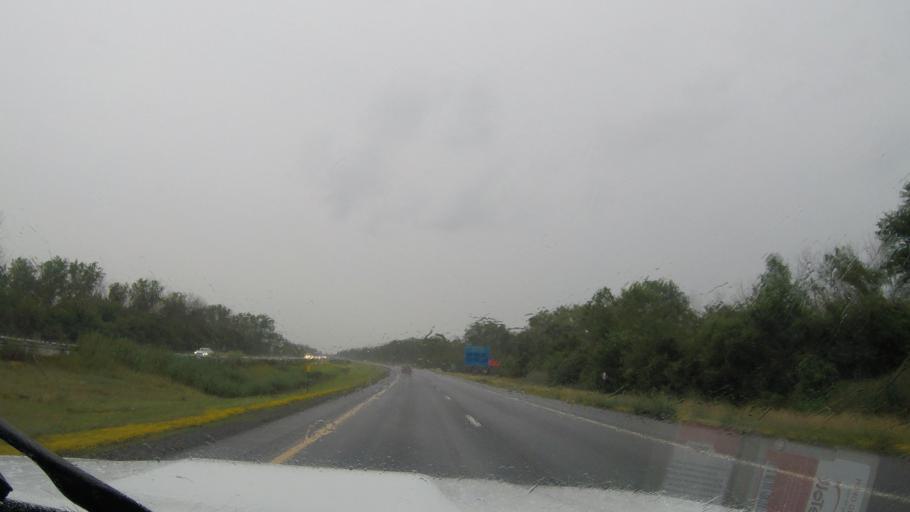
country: US
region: New York
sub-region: Cayuga County
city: Port Byron
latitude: 43.0081
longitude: -76.6996
